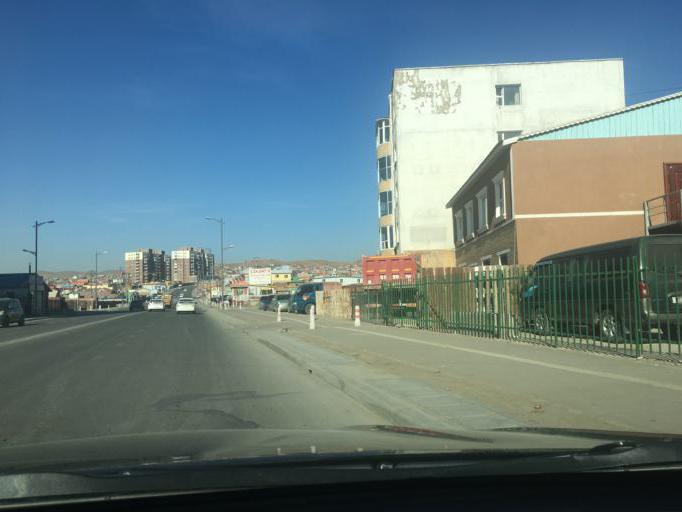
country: MN
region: Ulaanbaatar
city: Ulaanbaatar
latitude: 47.9114
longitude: 106.7840
